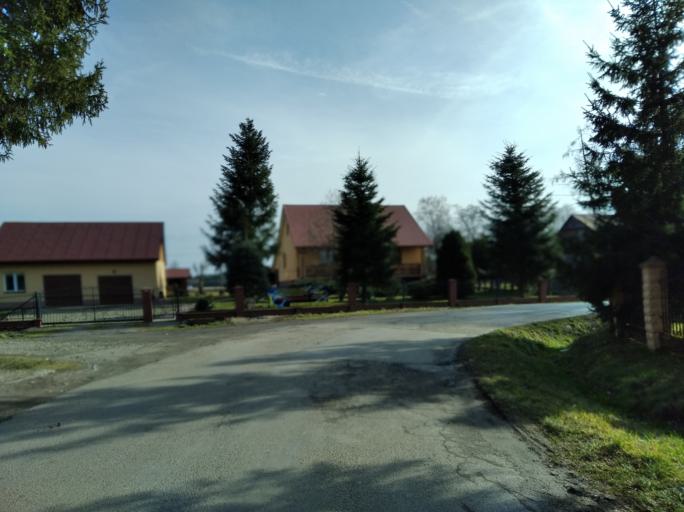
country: PL
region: Subcarpathian Voivodeship
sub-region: Powiat brzozowski
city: Humniska
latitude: 49.6682
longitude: 22.0547
